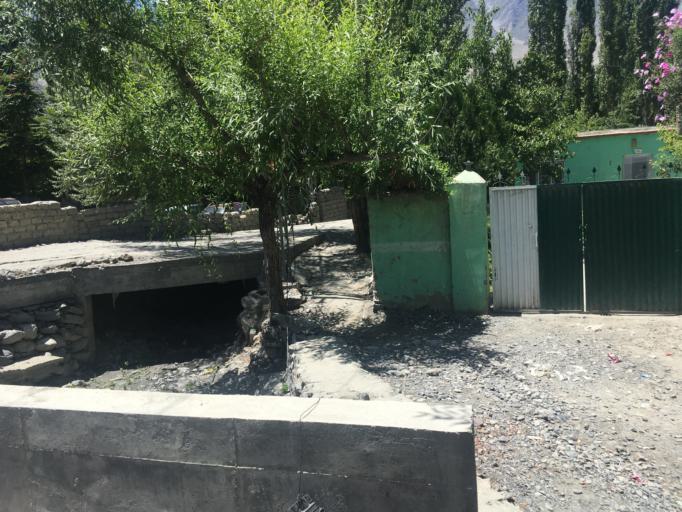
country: PK
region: Gilgit-Baltistan
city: Skardu
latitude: 35.3063
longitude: 75.5458
